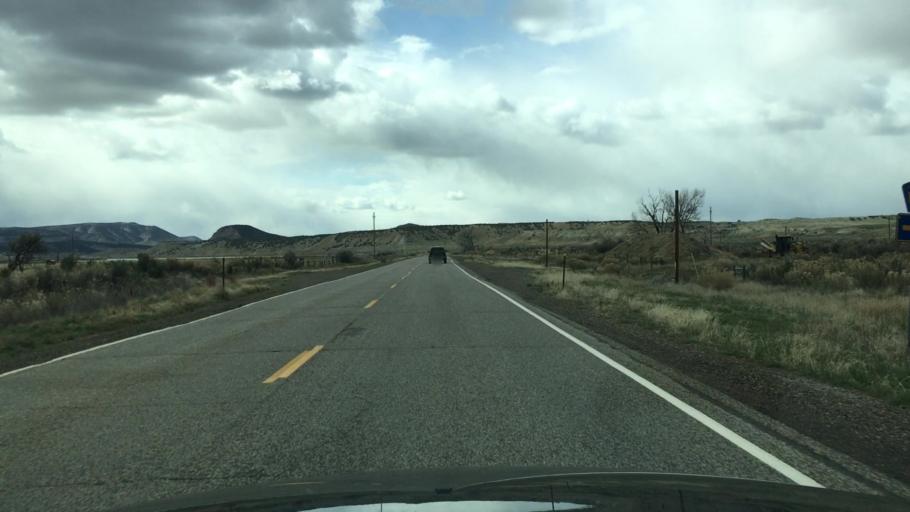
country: US
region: Colorado
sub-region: Rio Blanco County
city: Meeker
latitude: 40.0827
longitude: -108.1935
